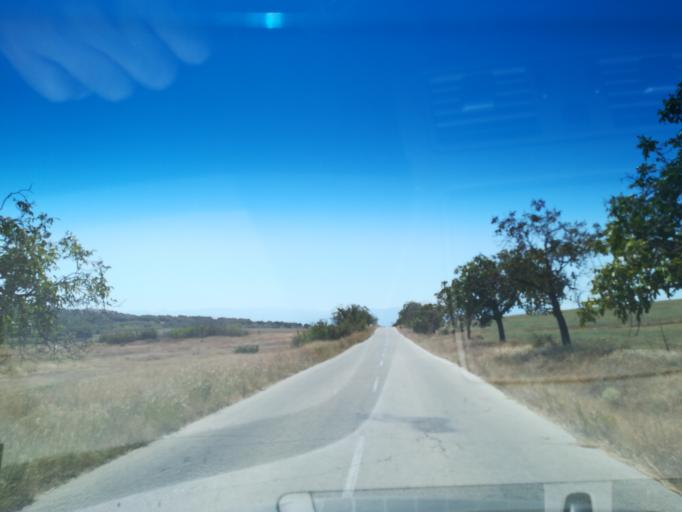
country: BG
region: Pazardzhik
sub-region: Obshtina Pazardzhik
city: Pazardzhik
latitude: 42.3176
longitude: 24.4065
